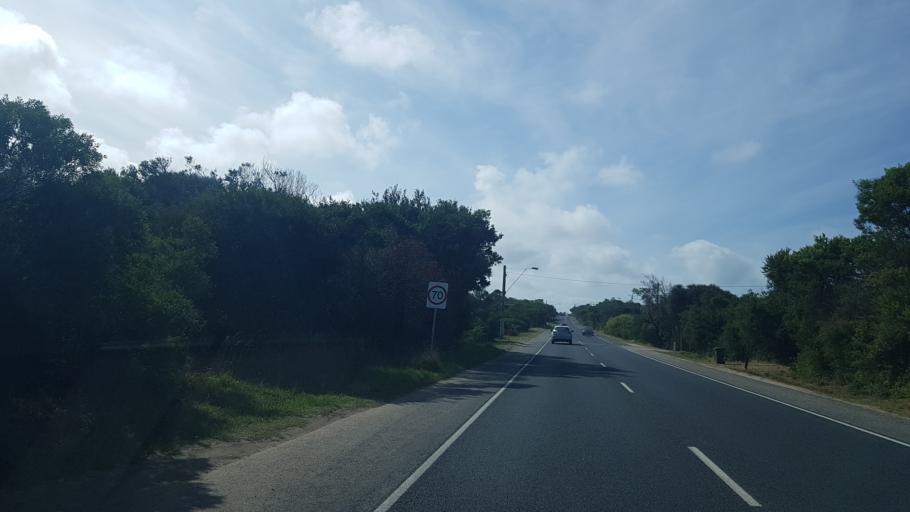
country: AU
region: Victoria
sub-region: Mornington Peninsula
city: Sorrento
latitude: -38.3508
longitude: 144.7466
